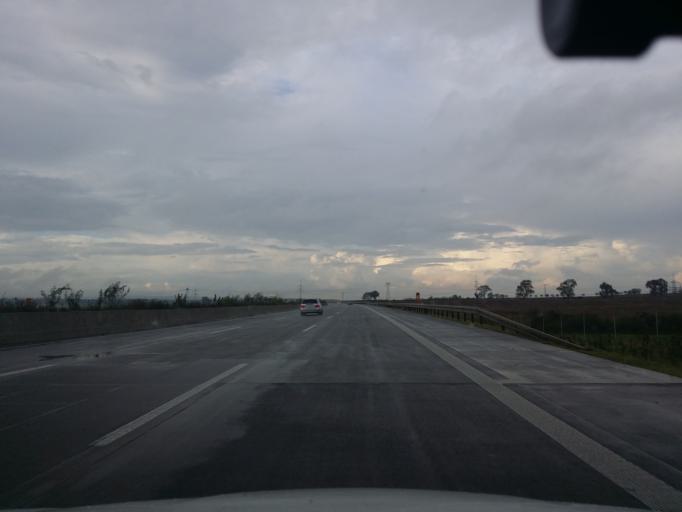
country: DE
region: Thuringia
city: Mechterstadt
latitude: 50.9615
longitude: 10.4882
